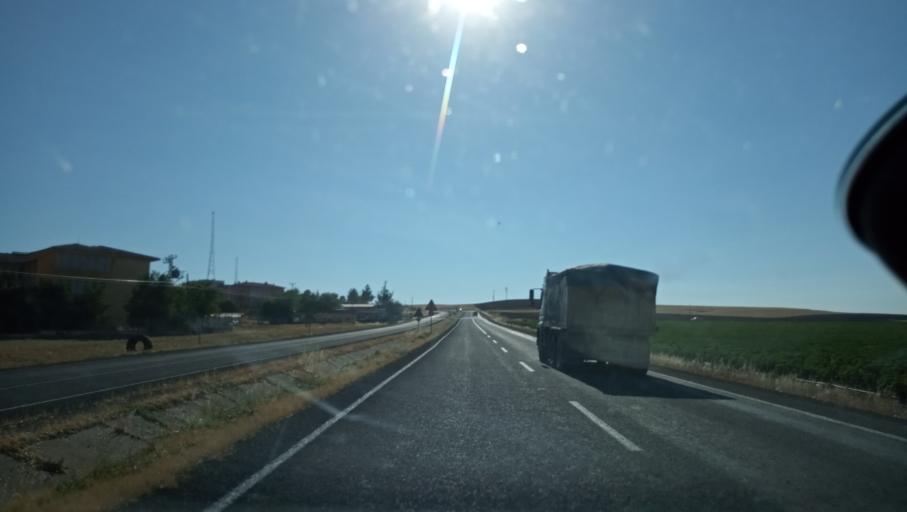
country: TR
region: Diyarbakir
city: Sur
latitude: 37.9911
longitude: 40.3879
